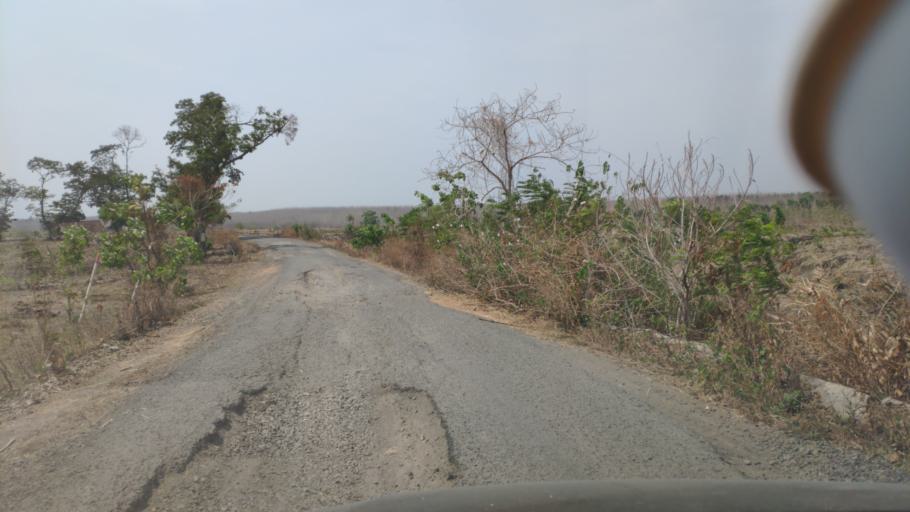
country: ID
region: Central Java
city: Pipes
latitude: -7.1483
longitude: 111.2732
